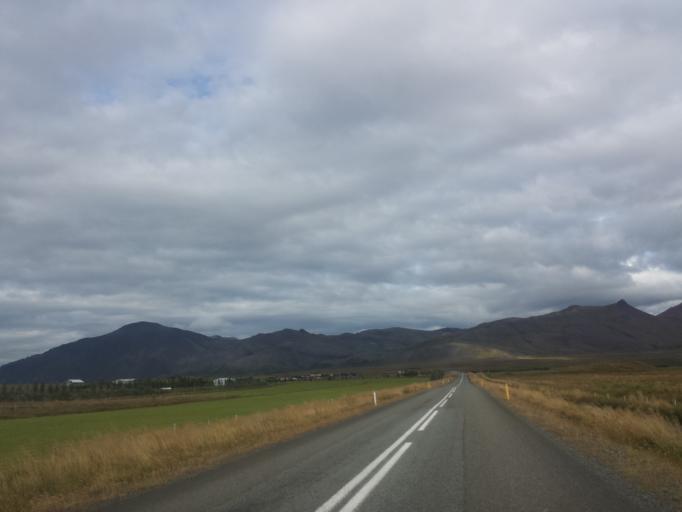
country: IS
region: West
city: Borgarnes
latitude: 64.4011
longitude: -21.8534
